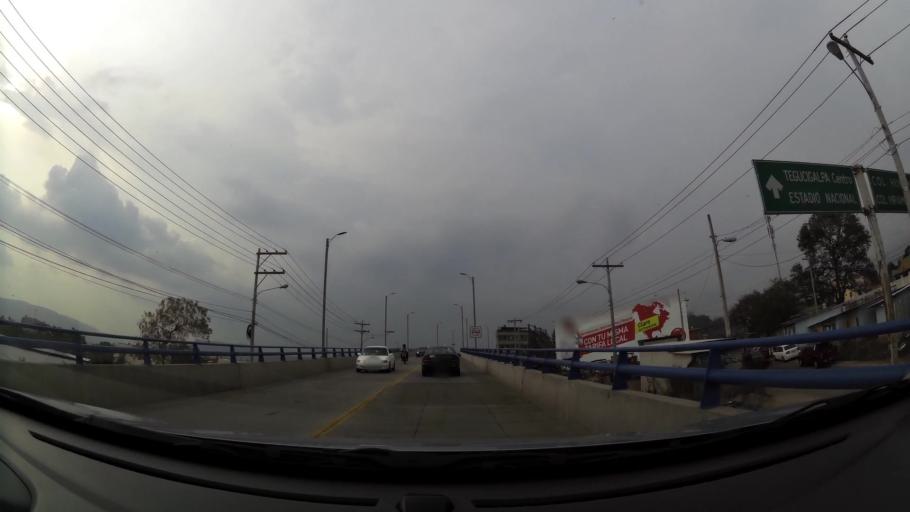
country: HN
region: Francisco Morazan
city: Tegucigalpa
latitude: 14.0841
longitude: -87.2037
